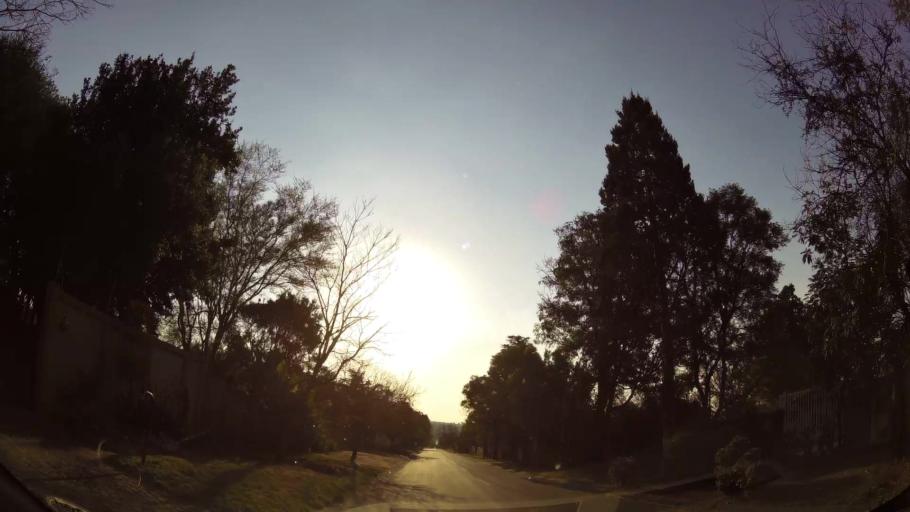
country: ZA
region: Gauteng
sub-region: City of Johannesburg Metropolitan Municipality
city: Diepsloot
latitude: -26.0628
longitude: 27.9887
